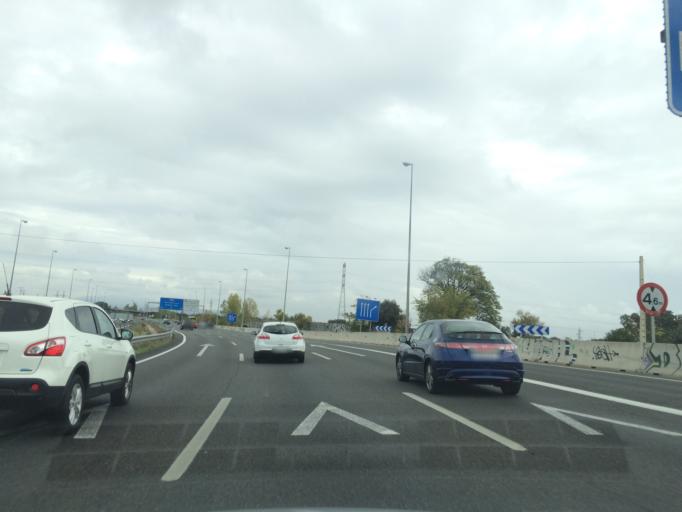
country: ES
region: Madrid
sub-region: Provincia de Madrid
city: Tres Cantos
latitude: 40.5784
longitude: -3.7057
